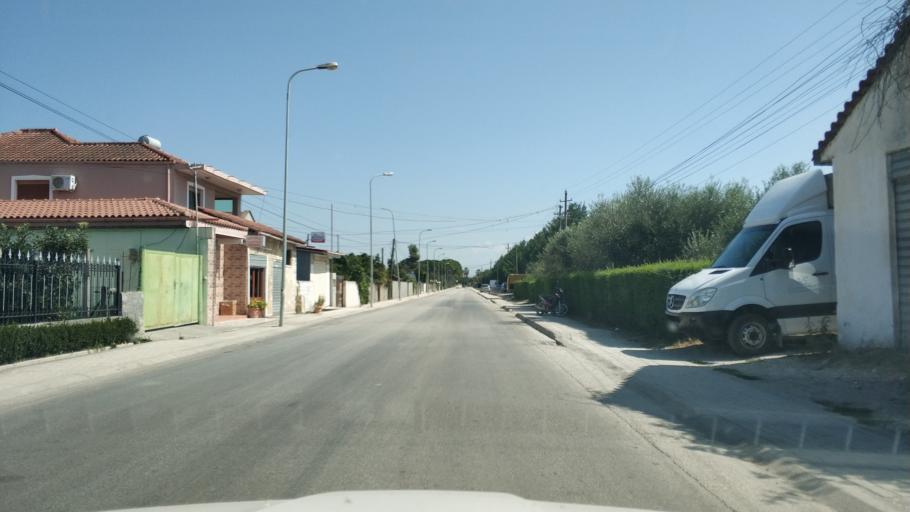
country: AL
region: Fier
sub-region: Rrethi i Lushnjes
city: Gradishte
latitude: 40.8937
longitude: 19.6262
